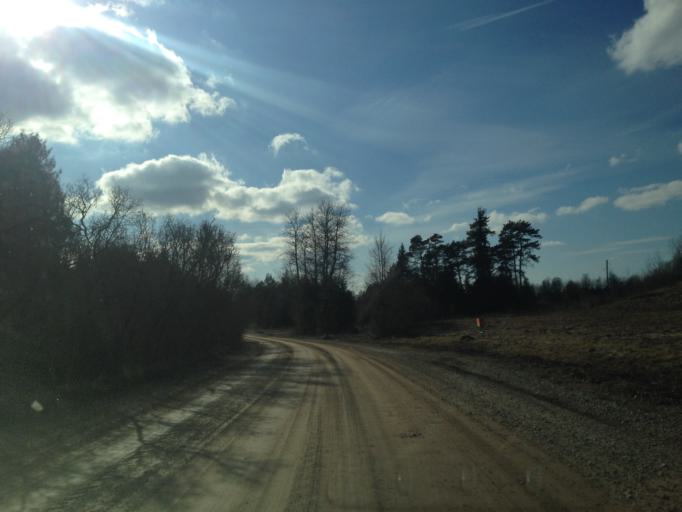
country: EE
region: Harju
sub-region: Nissi vald
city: Riisipere
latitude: 59.1251
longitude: 24.4363
